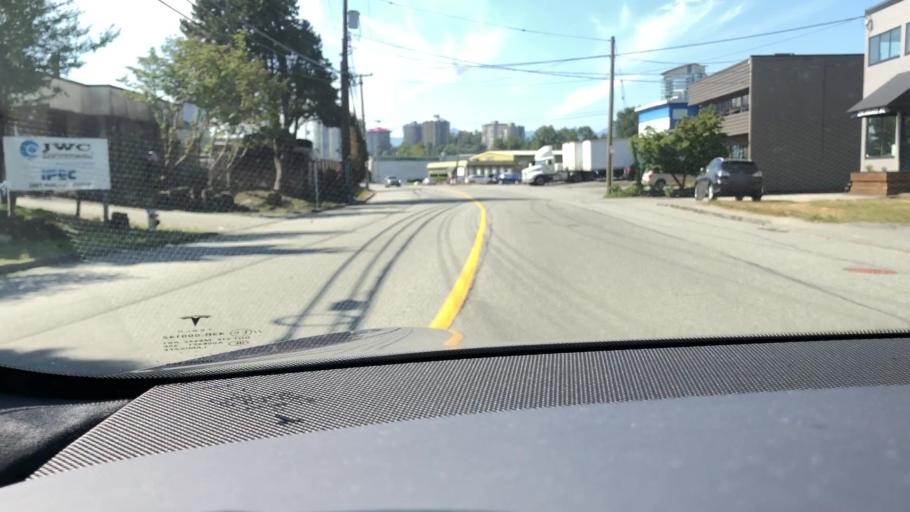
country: CA
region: British Columbia
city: Burnaby
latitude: 49.2577
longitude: -122.9779
